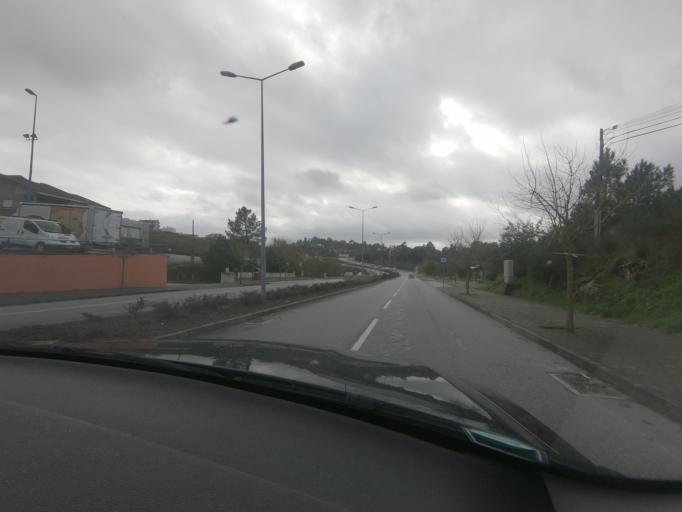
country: PT
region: Viseu
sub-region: Viseu
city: Abraveses
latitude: 40.6833
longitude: -7.9269
